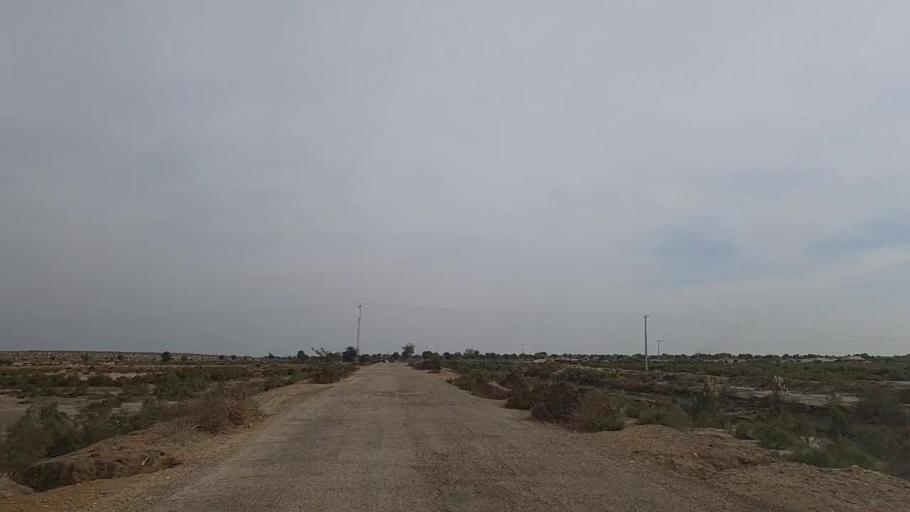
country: PK
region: Sindh
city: Jam Sahib
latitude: 26.4019
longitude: 68.5032
